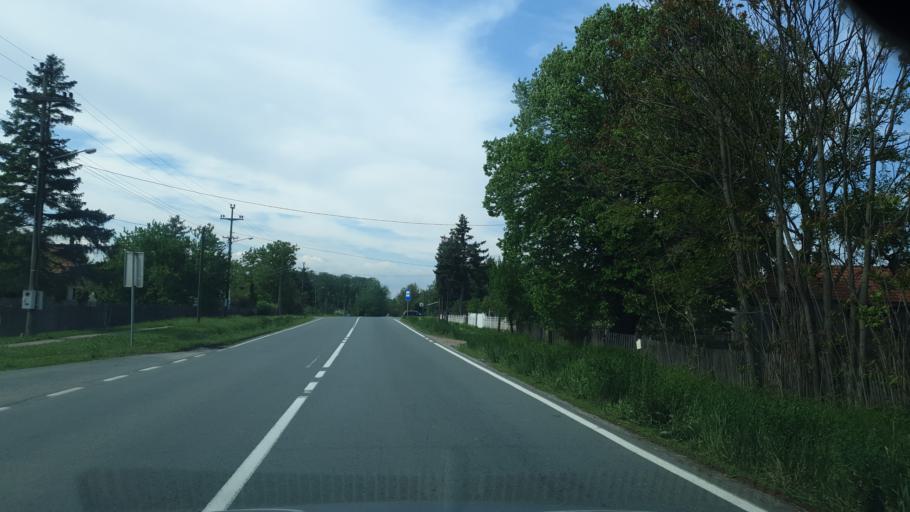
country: RS
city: Stubline
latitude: 44.5919
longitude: 20.1474
